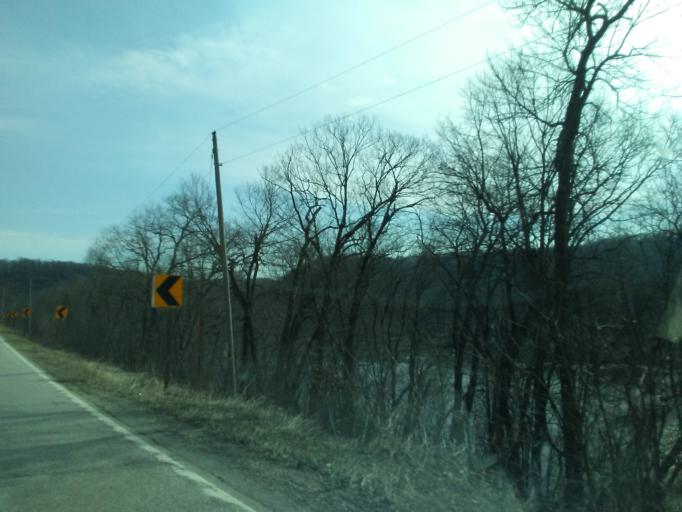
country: US
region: Wisconsin
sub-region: Crawford County
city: Prairie du Chien
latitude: 43.0903
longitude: -91.1931
